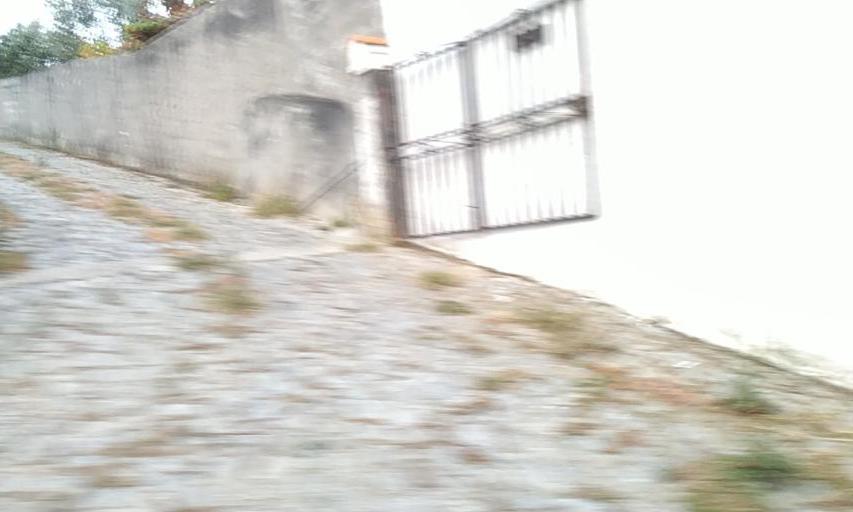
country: PT
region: Vila Real
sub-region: Mesao Frio
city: Mesao Frio
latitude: 41.1827
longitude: -7.8502
